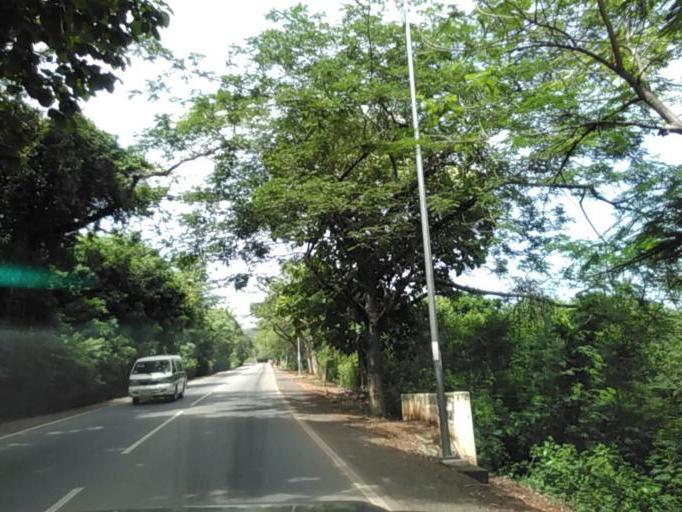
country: GH
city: Akropong
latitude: 6.2686
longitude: 0.0582
